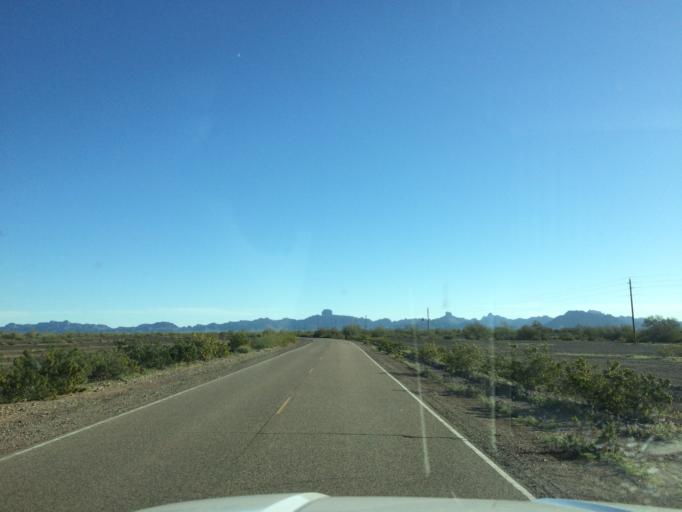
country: US
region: Arizona
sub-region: Yuma County
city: Wellton
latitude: 32.9711
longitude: -114.2822
